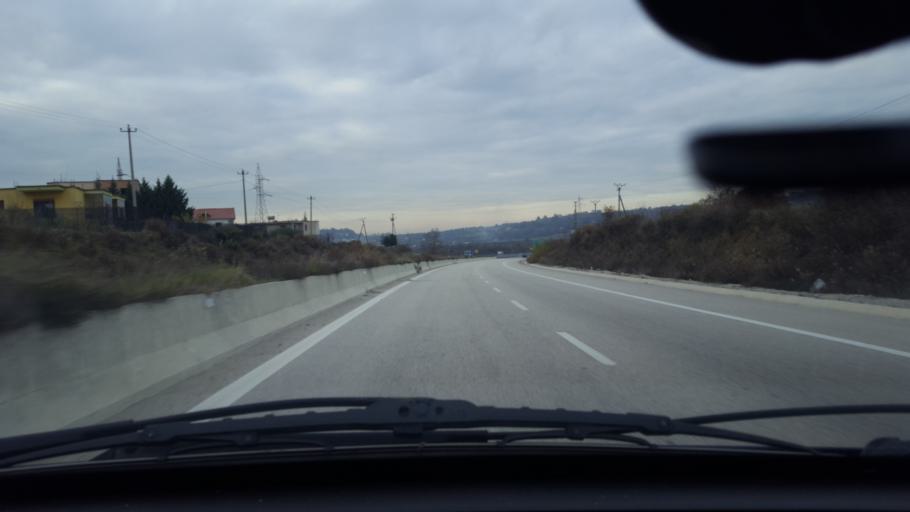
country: AL
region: Tirane
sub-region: Rrethi i Tiranes
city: Berzhite
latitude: 41.2524
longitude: 19.8950
